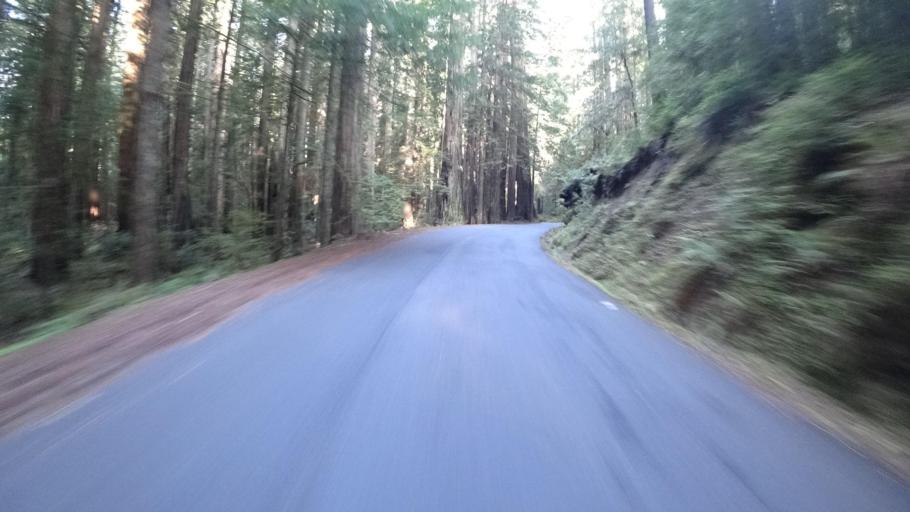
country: US
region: California
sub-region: Humboldt County
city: Rio Dell
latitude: 40.3514
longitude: -123.9690
